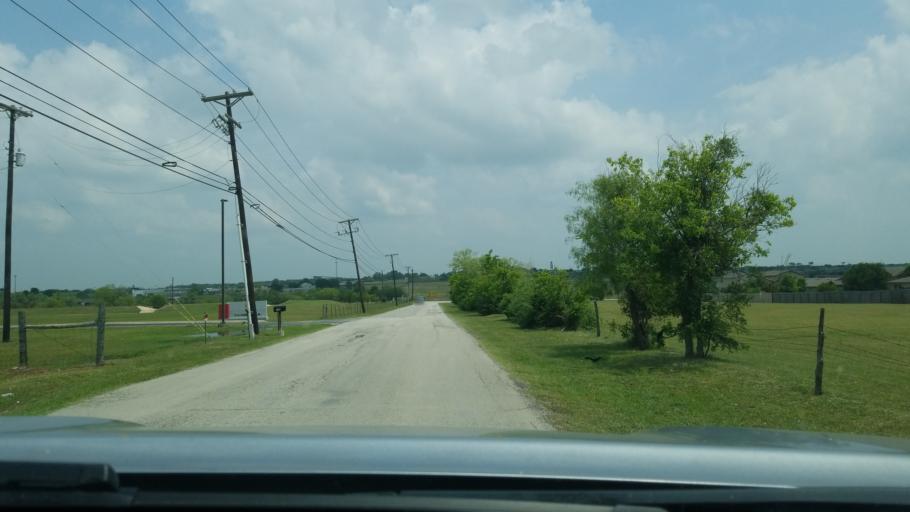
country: US
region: Texas
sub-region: Comal County
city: New Braunfels
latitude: 29.7588
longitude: -98.0663
